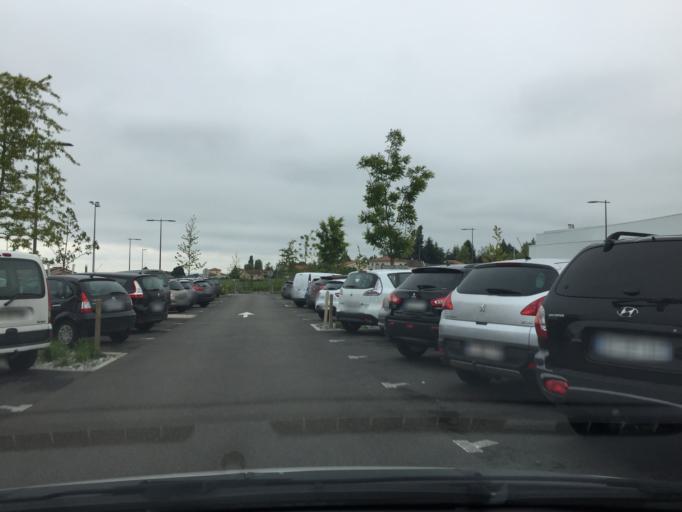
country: FR
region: Rhone-Alpes
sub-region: Departement du Rhone
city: Mornant
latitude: 45.6256
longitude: 4.6722
